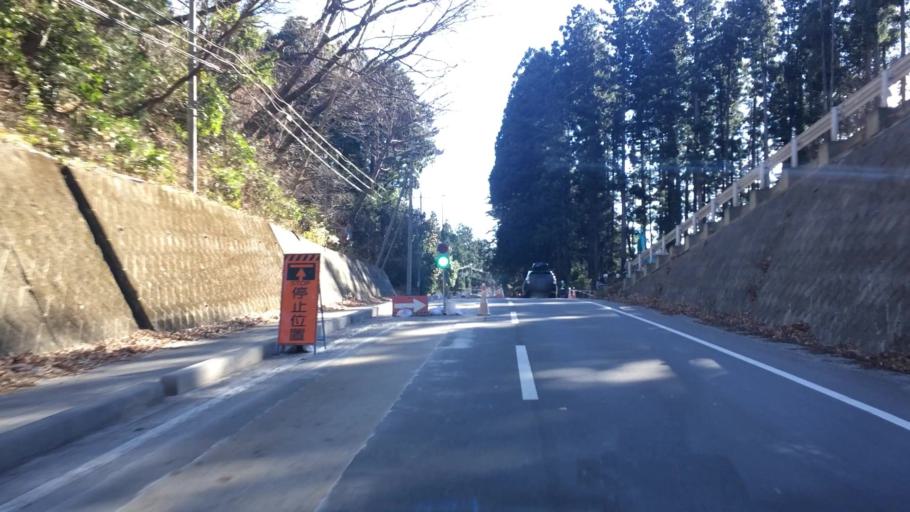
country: JP
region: Tochigi
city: Imaichi
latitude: 36.7307
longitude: 139.7474
